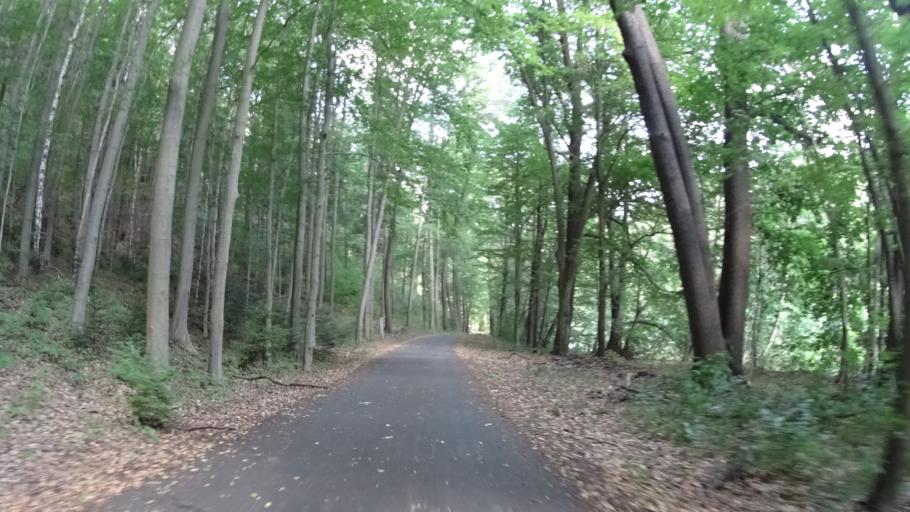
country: DE
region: Saxony
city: Schlegel
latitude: 50.9729
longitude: 14.9092
